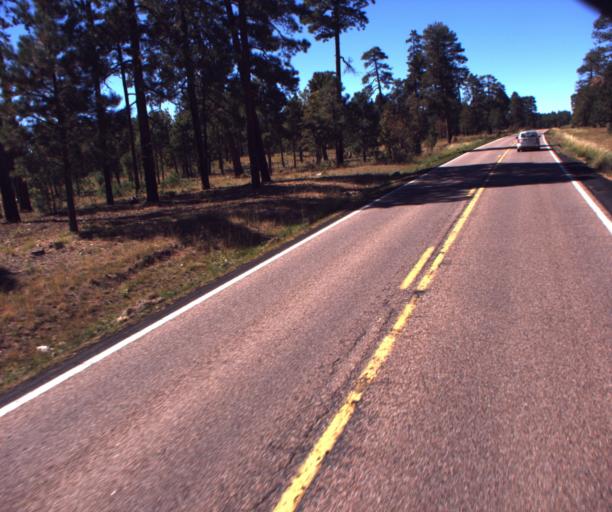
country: US
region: Arizona
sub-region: Navajo County
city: Heber-Overgaard
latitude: 34.3386
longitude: -110.7298
